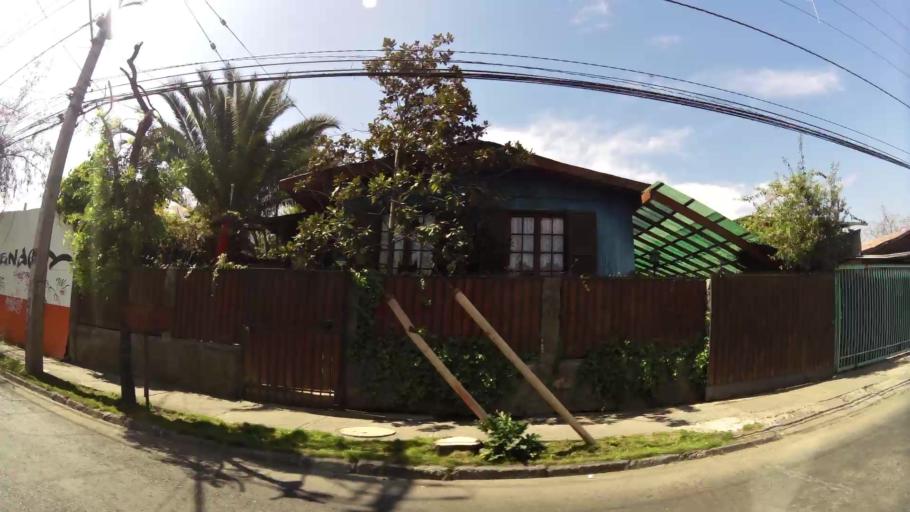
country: CL
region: Santiago Metropolitan
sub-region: Provincia de Santiago
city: Villa Presidente Frei, Nunoa, Santiago, Chile
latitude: -33.4684
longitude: -70.5319
